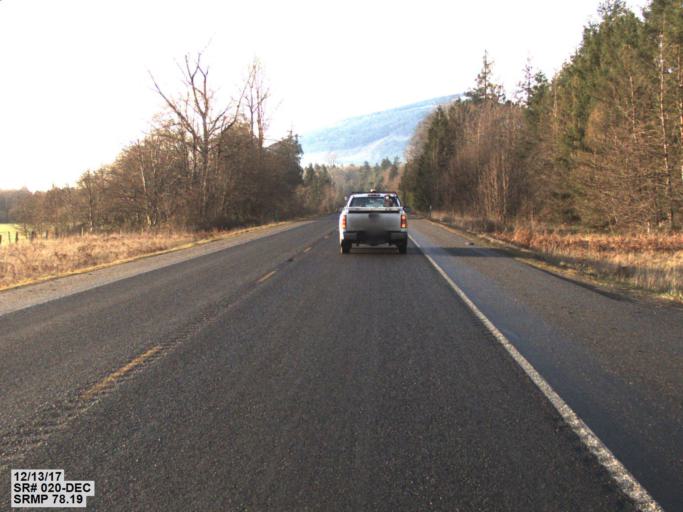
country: US
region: Washington
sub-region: Skagit County
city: Sedro-Woolley
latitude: 48.5277
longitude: -121.9734
